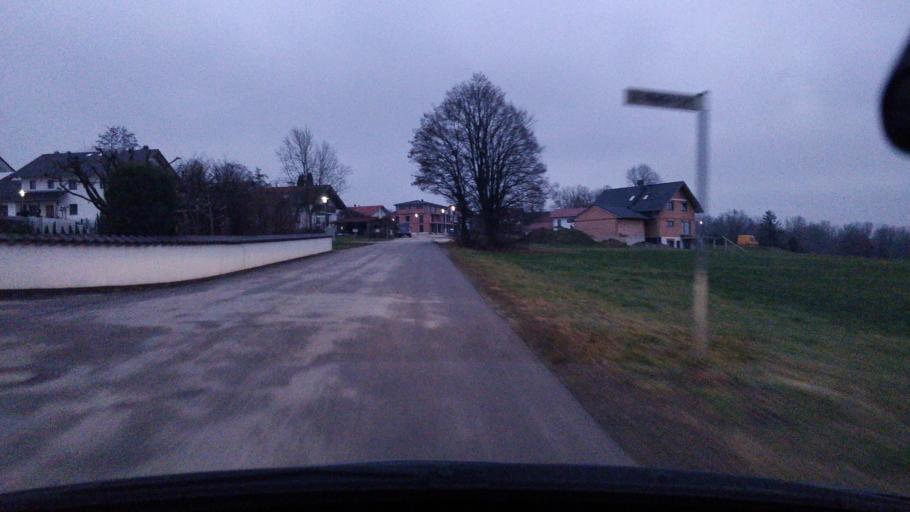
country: DE
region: Bavaria
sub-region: Upper Bavaria
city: Obertaufkirchen
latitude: 48.2616
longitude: 12.2749
